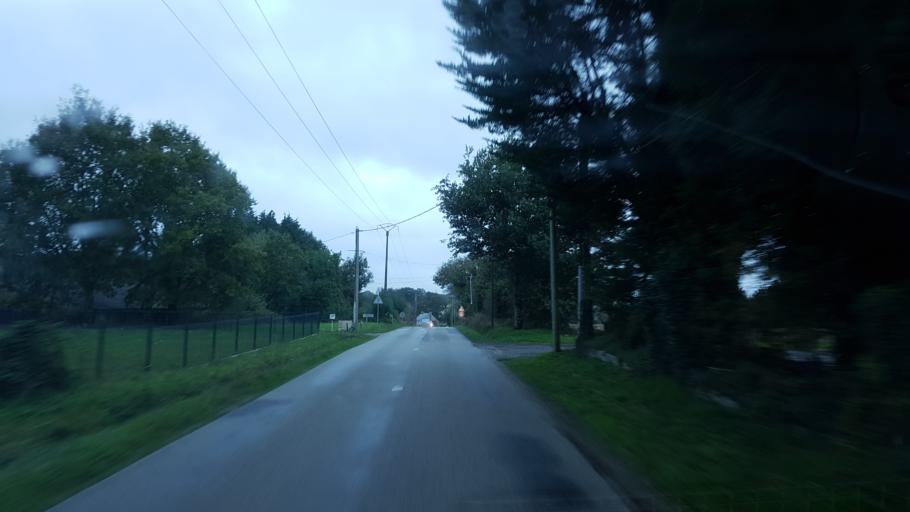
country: FR
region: Brittany
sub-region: Departement du Morbihan
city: Trefflean
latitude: 47.6766
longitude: -2.6008
